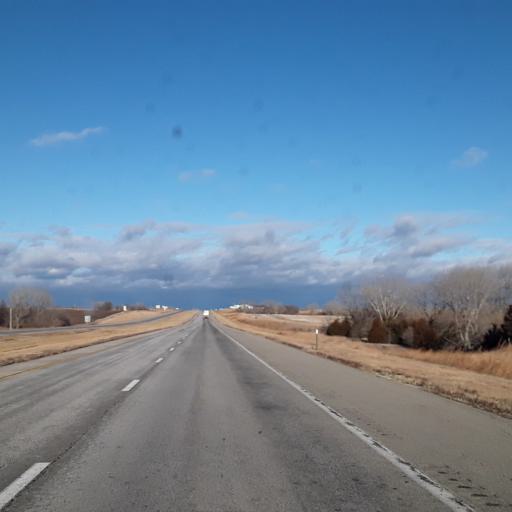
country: US
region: Kansas
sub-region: Republic County
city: Belleville
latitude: 39.8481
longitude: -97.6295
